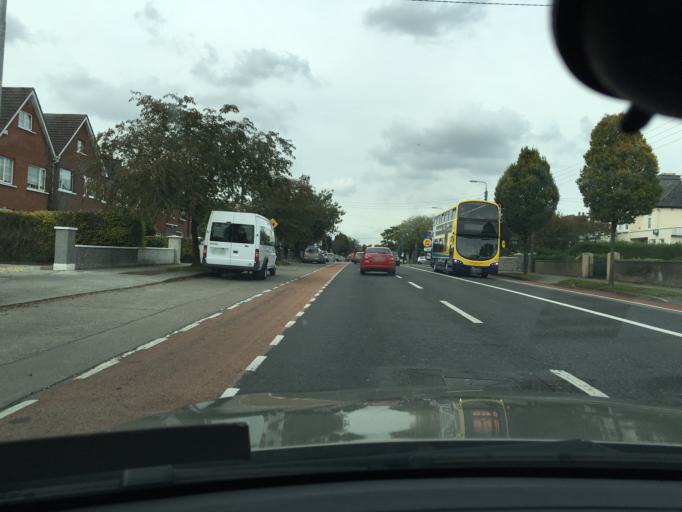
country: IE
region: Leinster
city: Cabra
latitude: 53.3657
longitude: -6.3108
